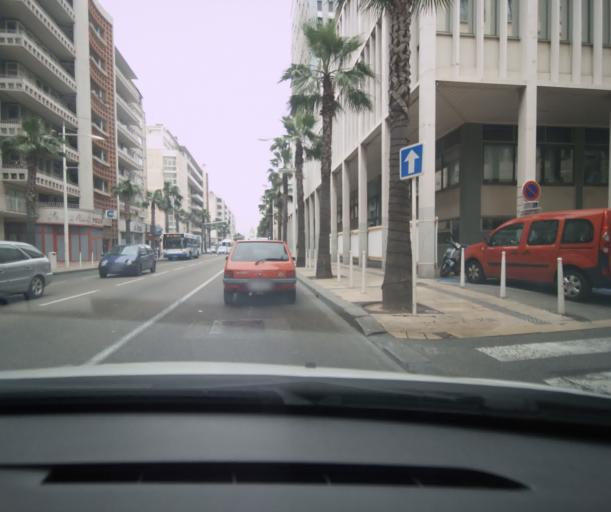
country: FR
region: Provence-Alpes-Cote d'Azur
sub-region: Departement du Var
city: Toulon
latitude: 43.1198
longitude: 5.9328
